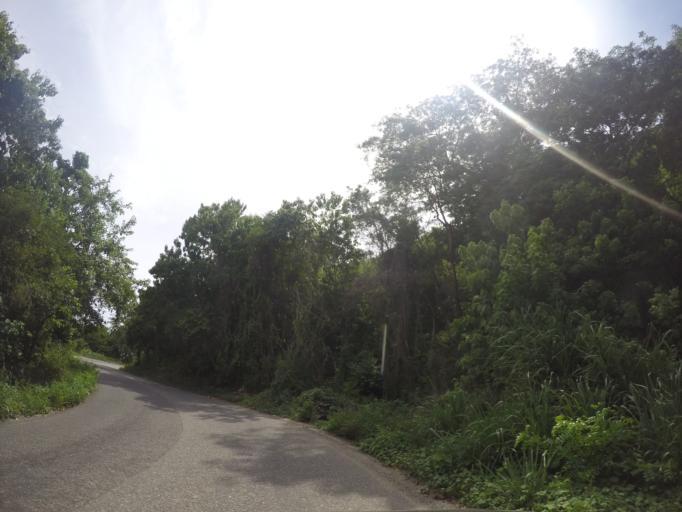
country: MX
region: Oaxaca
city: Santa Maria Tonameca
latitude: 15.6688
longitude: -96.5312
